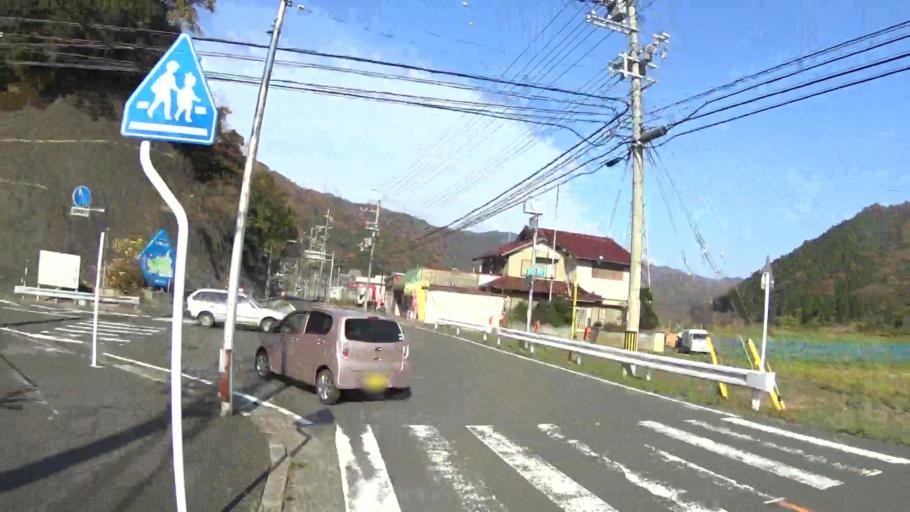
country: JP
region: Kyoto
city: Maizuru
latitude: 35.5163
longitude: 135.4023
